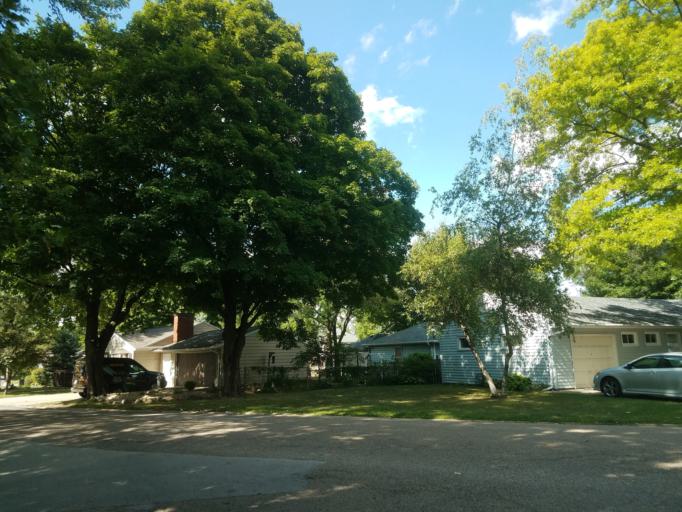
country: US
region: Illinois
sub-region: McLean County
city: Bloomington
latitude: 40.4842
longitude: -88.9814
